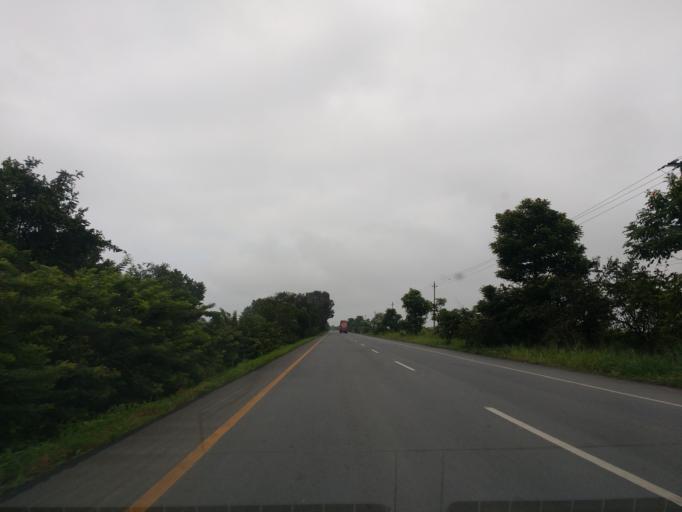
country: CO
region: Valle del Cauca
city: Palmira
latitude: 3.5538
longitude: -76.3369
